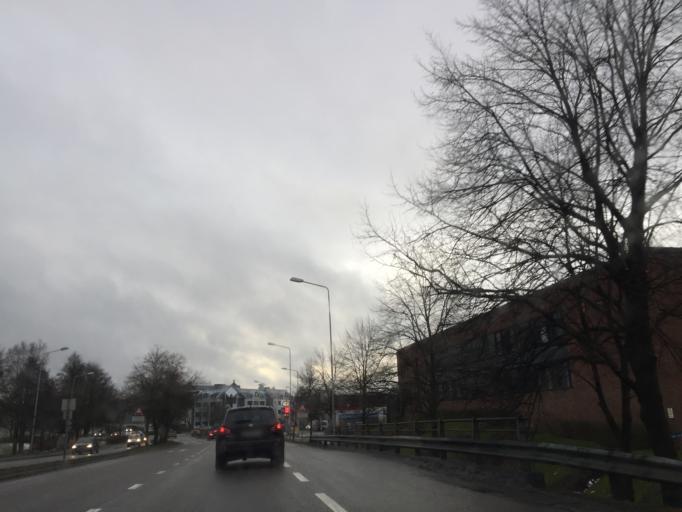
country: NO
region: Ostfold
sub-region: Moss
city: Moss
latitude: 59.4362
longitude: 10.6711
